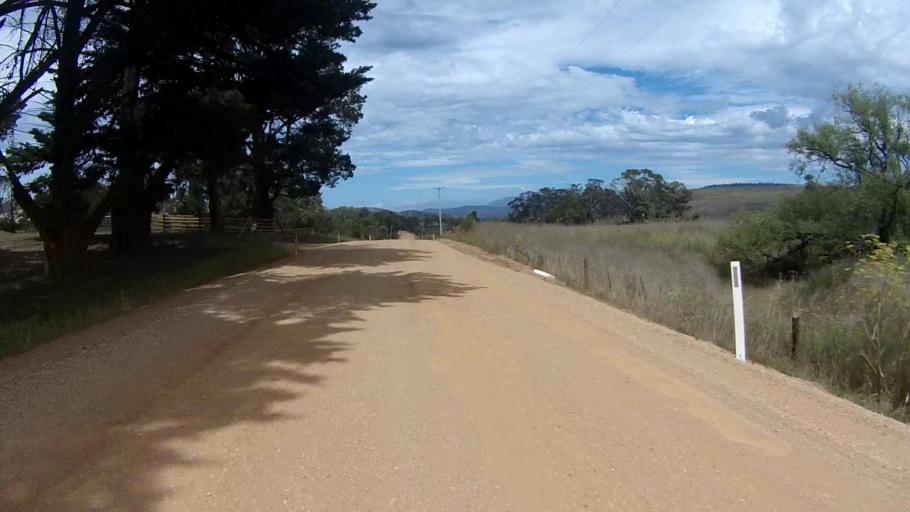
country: AU
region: Tasmania
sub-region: Sorell
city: Sorell
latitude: -42.6924
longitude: 147.4655
